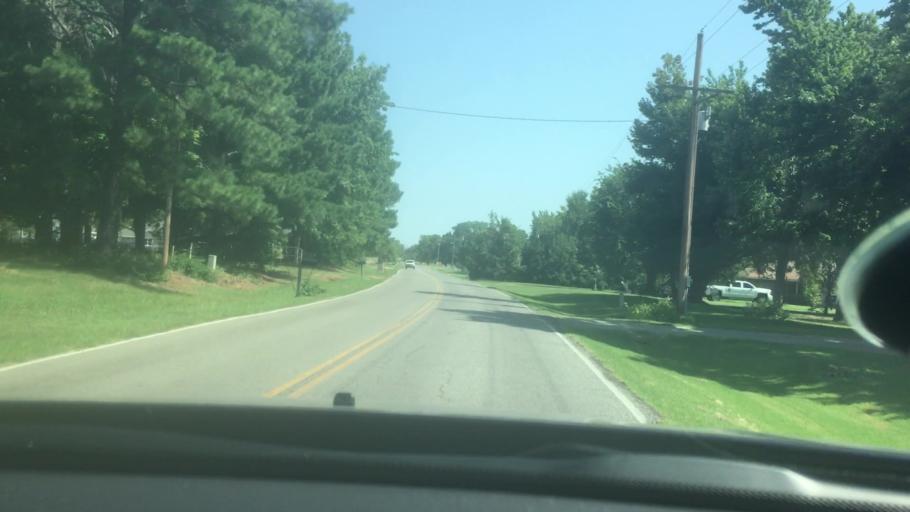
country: US
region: Oklahoma
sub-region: Bryan County
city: Calera
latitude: 34.0315
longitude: -96.4741
